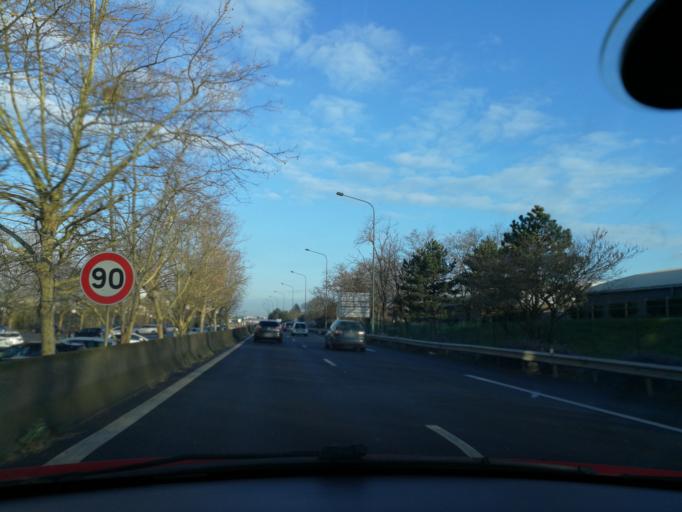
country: FR
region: Midi-Pyrenees
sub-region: Departement de la Haute-Garonne
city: Blagnac
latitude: 43.6329
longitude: 1.3806
